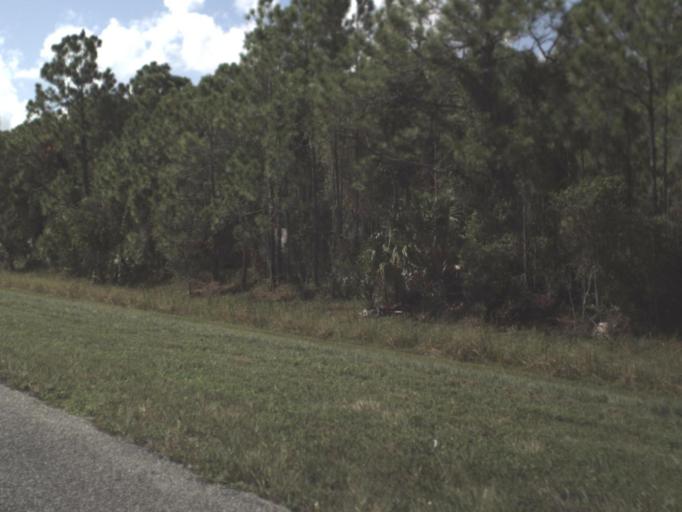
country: US
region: Florida
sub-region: Lee County
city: Burnt Store Marina
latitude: 26.8255
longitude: -81.9670
